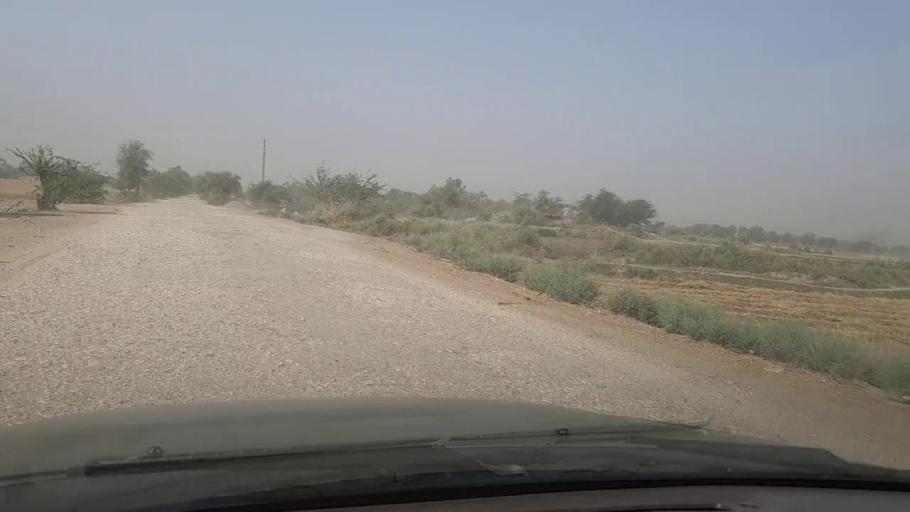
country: PK
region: Sindh
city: Shikarpur
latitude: 27.9069
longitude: 68.5984
